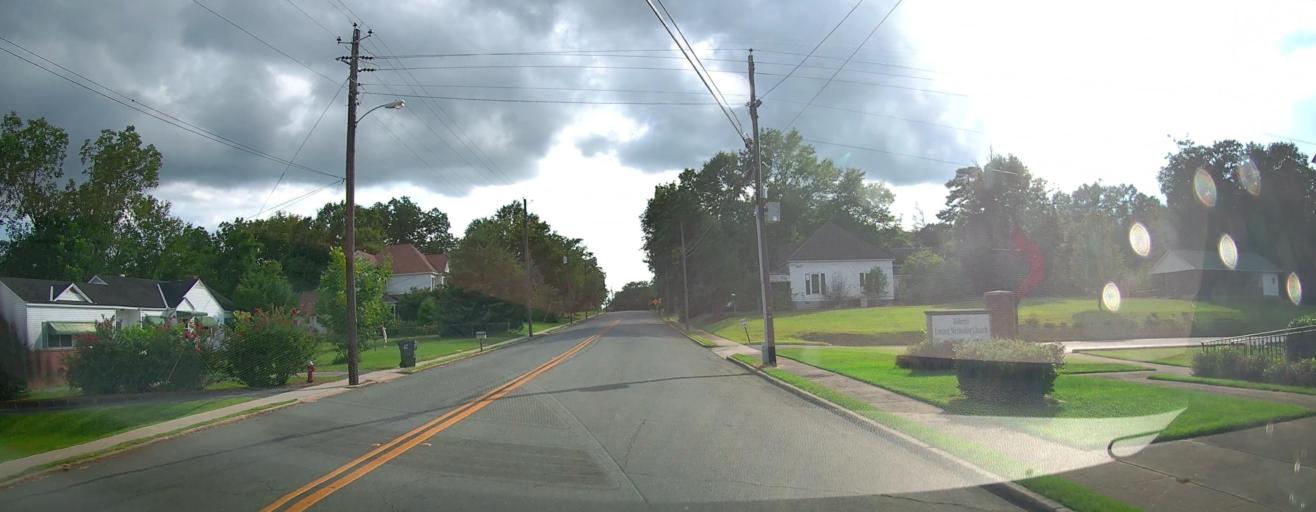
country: US
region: Georgia
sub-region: Crawford County
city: Roberta
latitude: 32.7183
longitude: -84.0130
